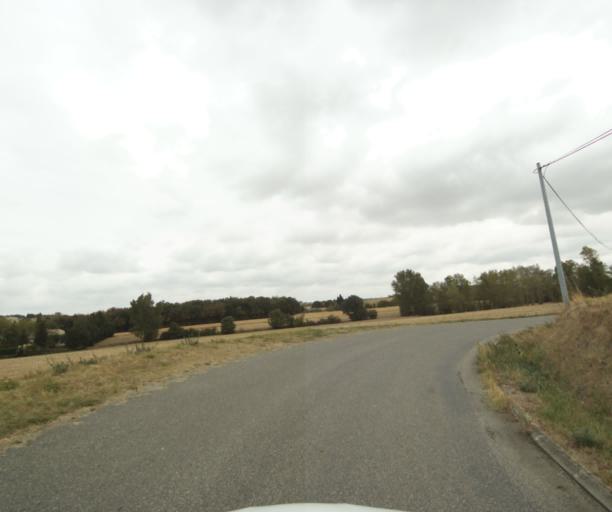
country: FR
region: Midi-Pyrenees
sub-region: Departement de la Haute-Garonne
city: Villefranche-de-Lauragais
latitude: 43.4128
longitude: 1.7403
